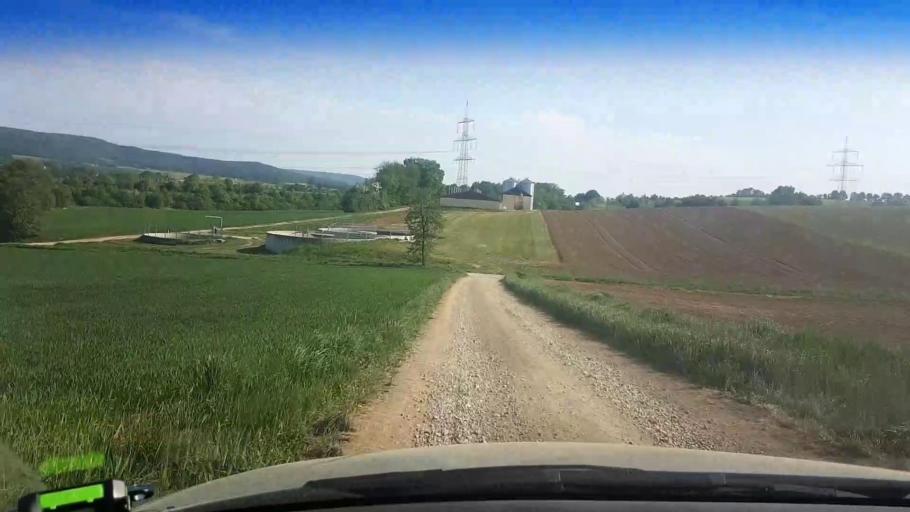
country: DE
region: Bavaria
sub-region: Upper Franconia
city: Memmelsdorf
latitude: 49.9663
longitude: 10.9850
